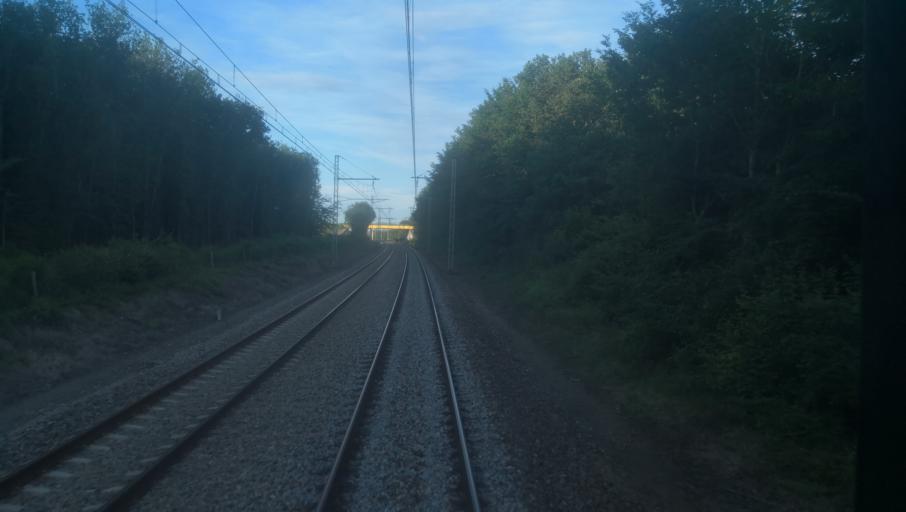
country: FR
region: Centre
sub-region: Departement de l'Indre
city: Saint-Maur
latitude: 46.7737
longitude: 1.6297
